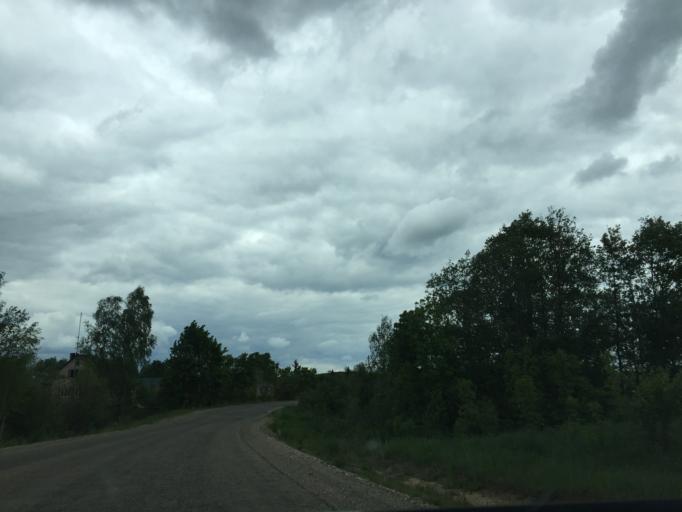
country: LV
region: Dagda
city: Dagda
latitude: 56.0844
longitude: 27.5313
